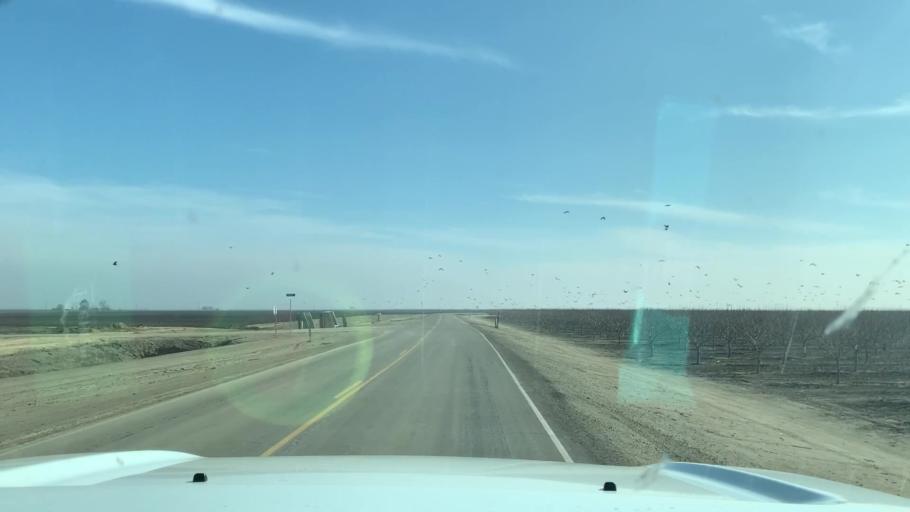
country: US
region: California
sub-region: Kern County
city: Buttonwillow
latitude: 35.4540
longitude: -119.5658
